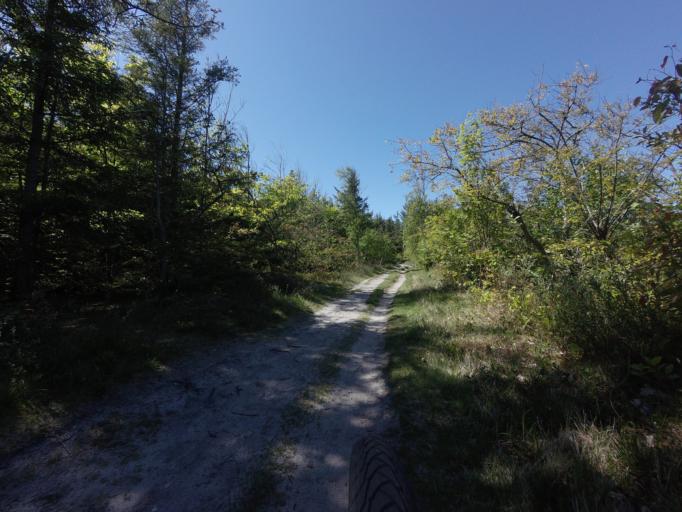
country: DK
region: North Denmark
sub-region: Jammerbugt Kommune
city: Pandrup
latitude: 57.2867
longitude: 9.6401
